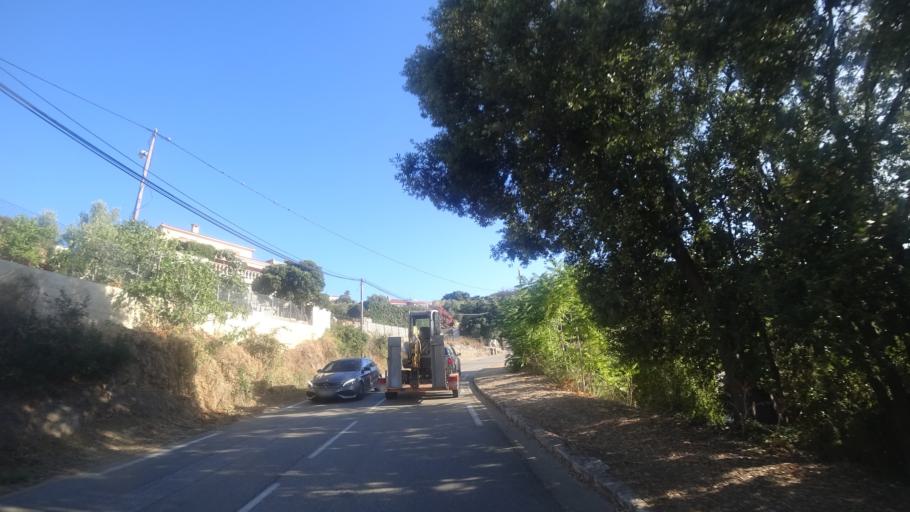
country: FR
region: Corsica
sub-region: Departement de la Corse-du-Sud
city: Cargese
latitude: 42.1390
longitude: 8.5999
